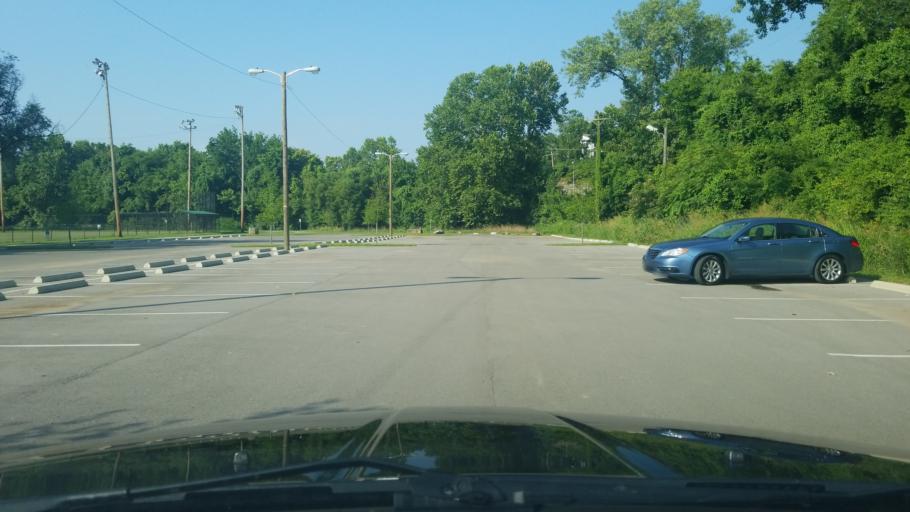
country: US
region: Tennessee
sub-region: Davidson County
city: Belle Meade
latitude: 36.1614
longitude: -86.8652
